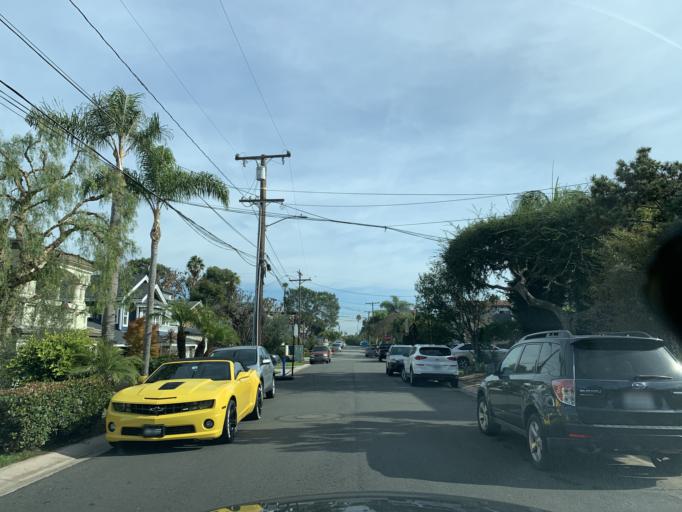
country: US
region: California
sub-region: Los Angeles County
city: Manhattan Beach
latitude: 33.8810
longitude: -118.3947
